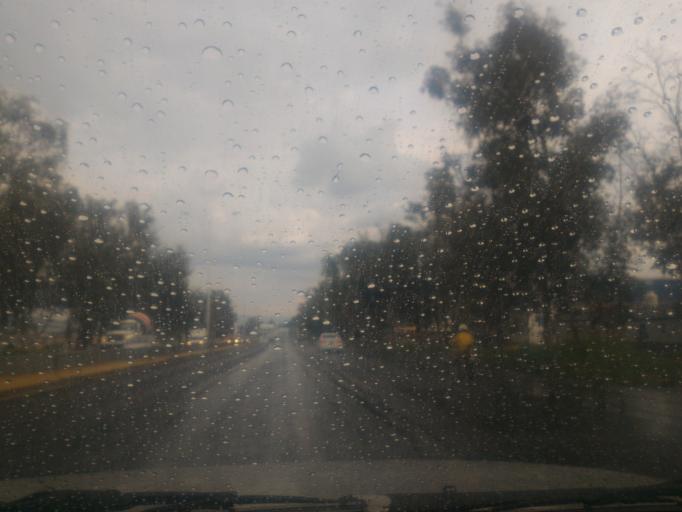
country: MX
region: Jalisco
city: Guadalajara
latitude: 20.6532
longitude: -103.4454
